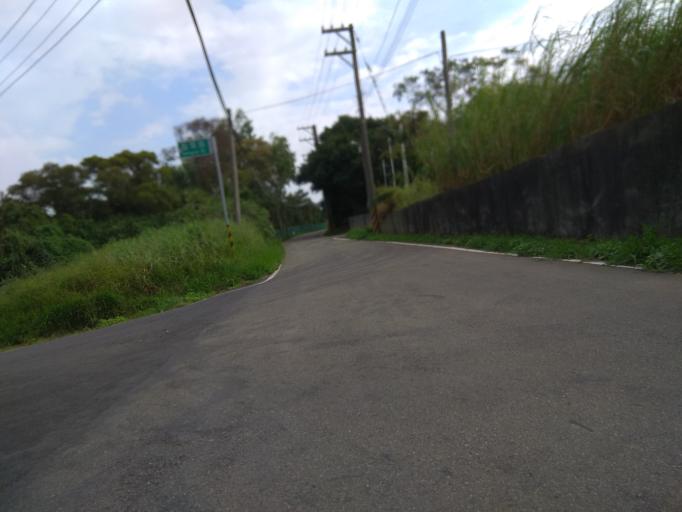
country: TW
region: Taiwan
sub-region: Hsinchu
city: Zhubei
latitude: 24.9740
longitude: 121.0237
